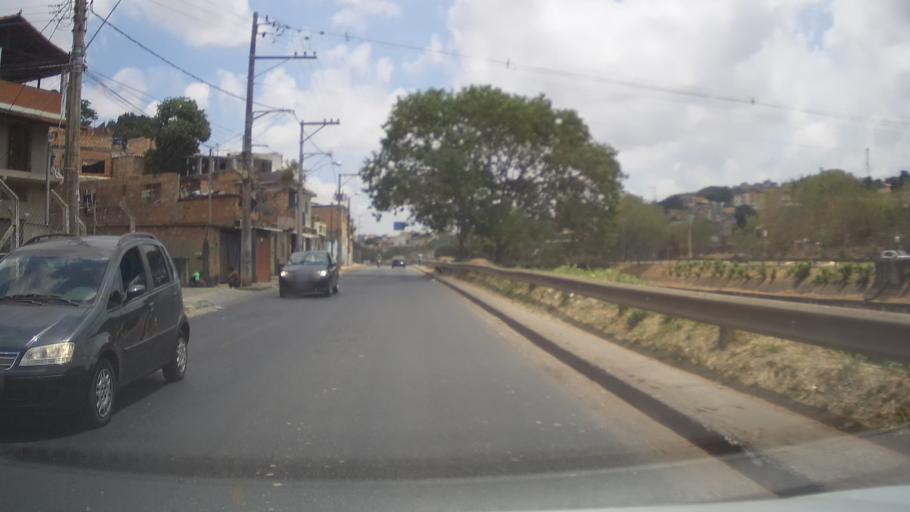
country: BR
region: Minas Gerais
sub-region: Belo Horizonte
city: Belo Horizonte
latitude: -19.9058
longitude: -43.8882
